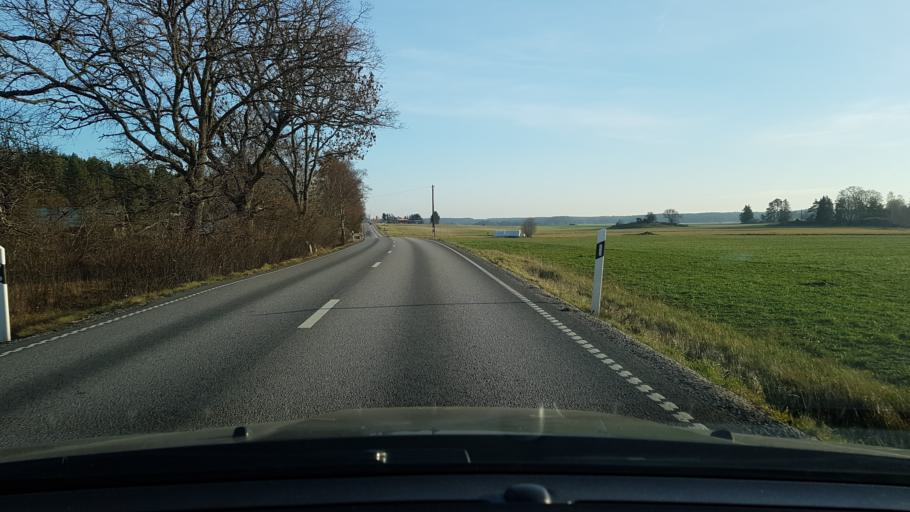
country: SE
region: Stockholm
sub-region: Norrtalje Kommun
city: Nykvarn
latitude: 59.7409
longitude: 18.1484
